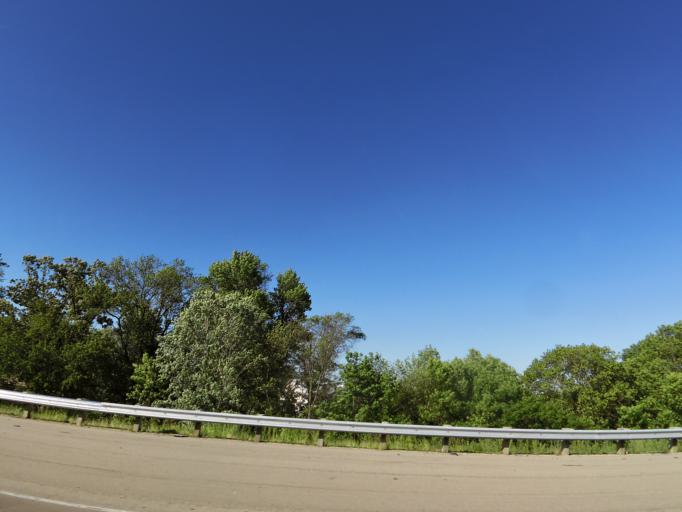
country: US
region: Wisconsin
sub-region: Dane County
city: McFarland
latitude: 43.0273
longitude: -89.2558
